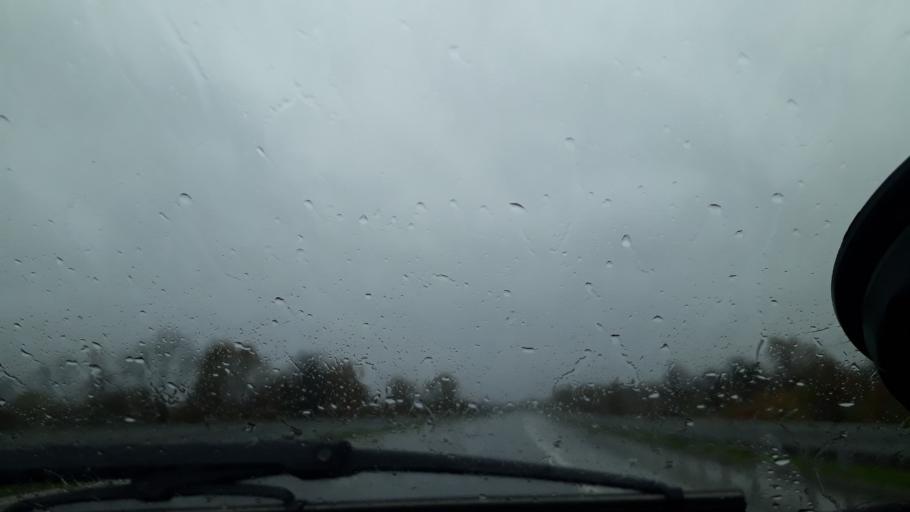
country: BA
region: Republika Srpska
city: Stanari
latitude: 44.8274
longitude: 17.8103
